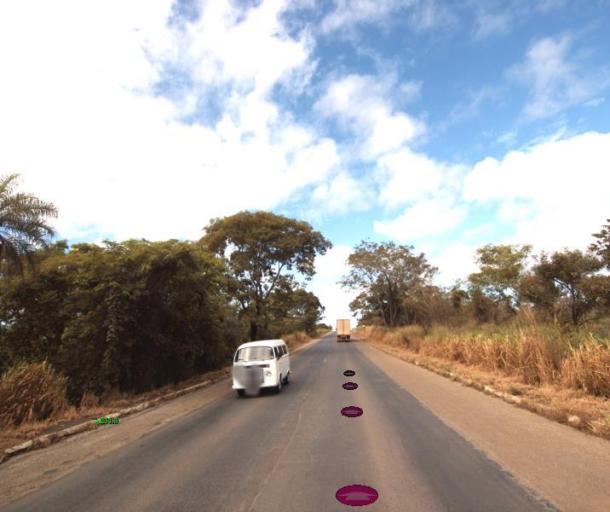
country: BR
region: Goias
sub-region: Uruacu
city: Uruacu
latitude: -14.7768
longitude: -49.2699
